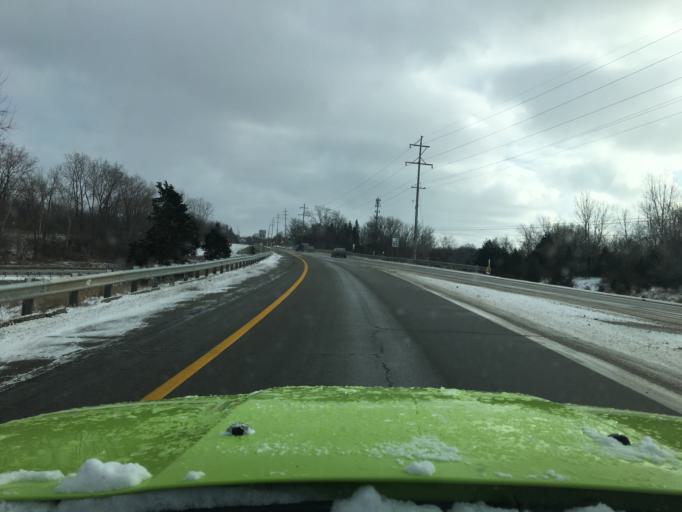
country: US
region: Michigan
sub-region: Kent County
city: East Grand Rapids
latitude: 42.9623
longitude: -85.5796
